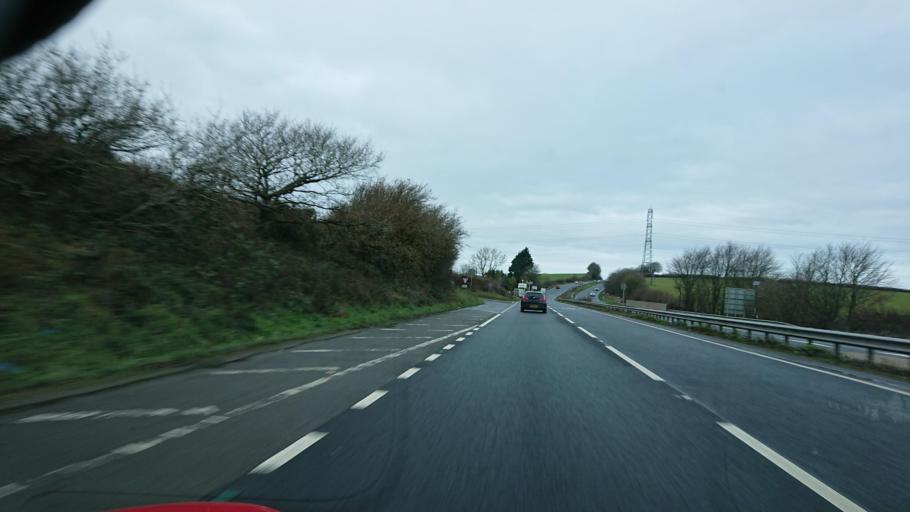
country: GB
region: England
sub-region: Cornwall
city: Liskeard
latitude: 50.4340
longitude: -4.4383
